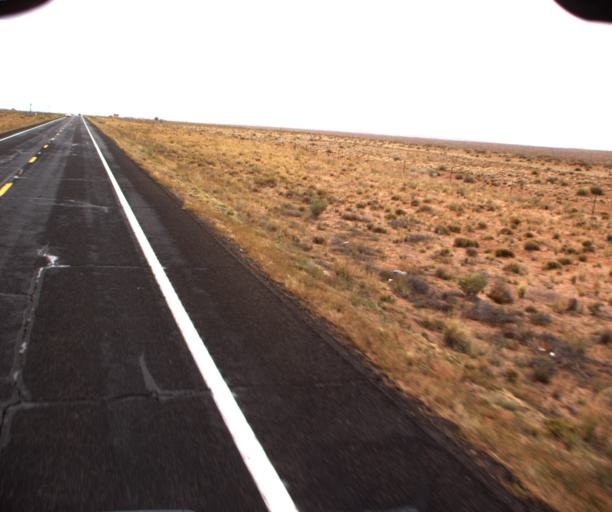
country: US
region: Arizona
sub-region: Coconino County
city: Tuba City
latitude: 36.1519
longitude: -111.1303
